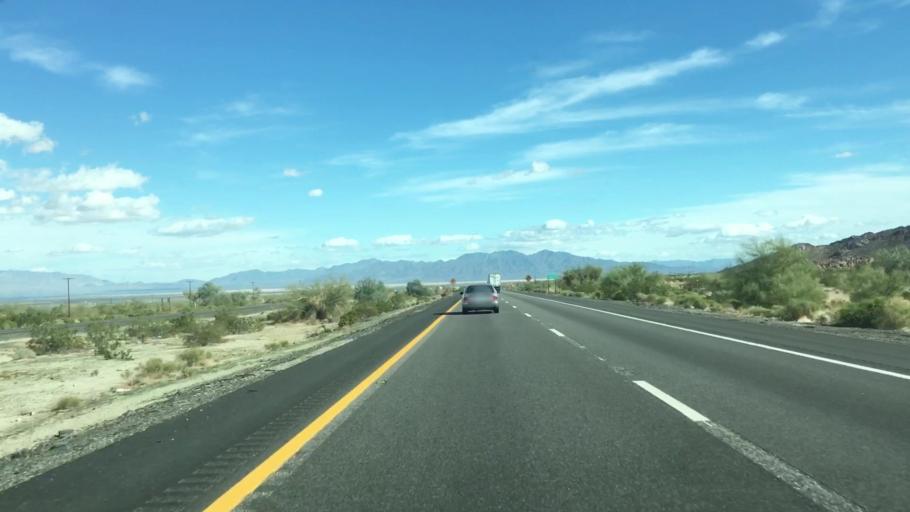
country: US
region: California
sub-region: Imperial County
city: Niland
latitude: 33.7090
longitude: -115.4244
